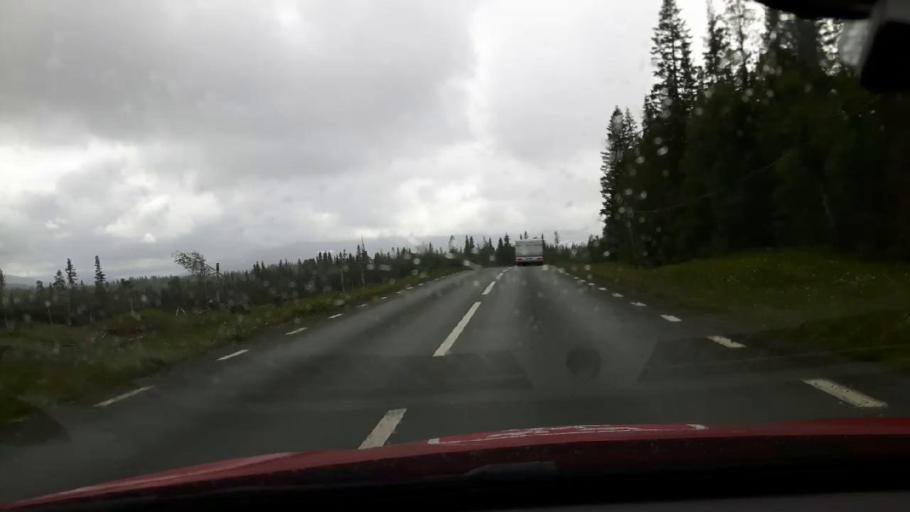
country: SE
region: Jaemtland
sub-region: Are Kommun
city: Are
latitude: 63.3123
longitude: 12.4837
